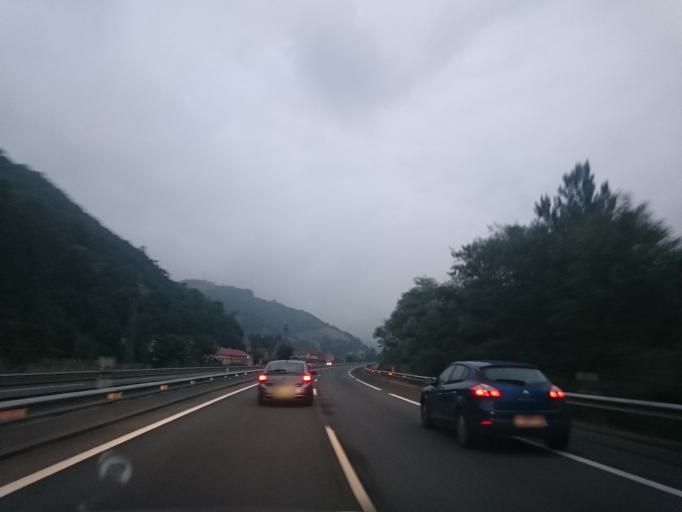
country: ES
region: Asturias
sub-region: Province of Asturias
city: Mieres
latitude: 43.2183
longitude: -5.7836
